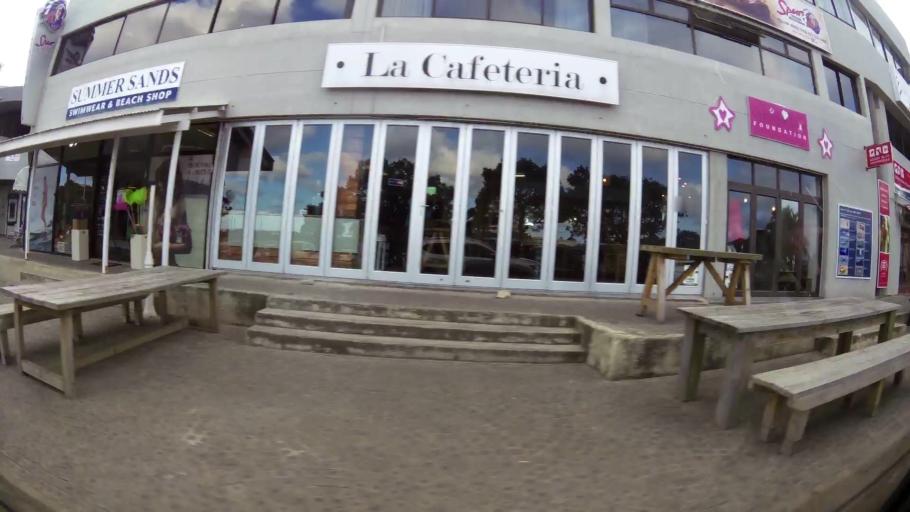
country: ZA
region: Western Cape
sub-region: Eden District Municipality
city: Plettenberg Bay
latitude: -34.0598
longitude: 23.3768
